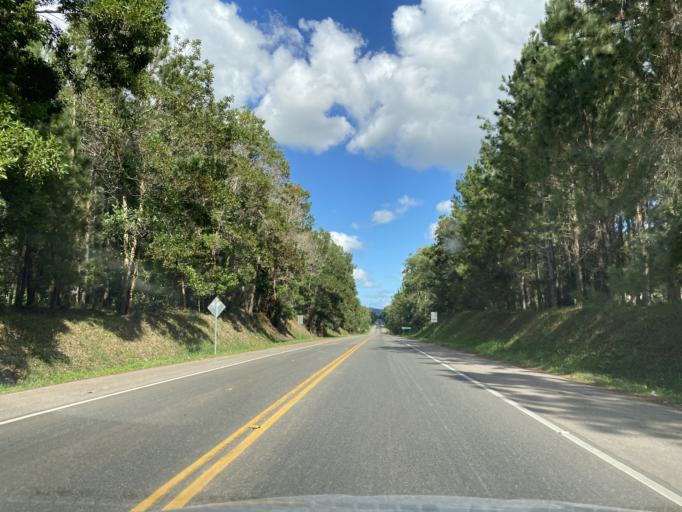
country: DO
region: Monte Plata
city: Monte Plata
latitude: 18.7696
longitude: -69.7537
